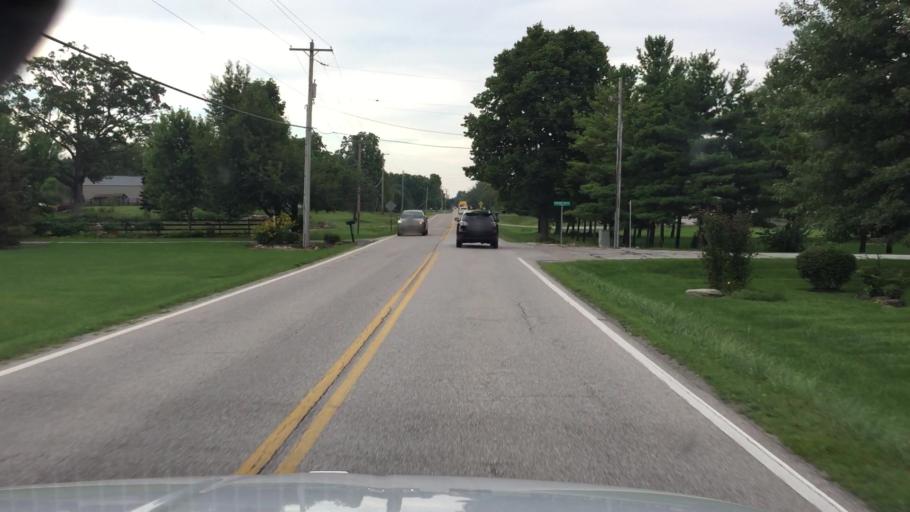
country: US
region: Ohio
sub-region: Franklin County
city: Lake Darby
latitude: 40.0054
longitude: -83.2622
